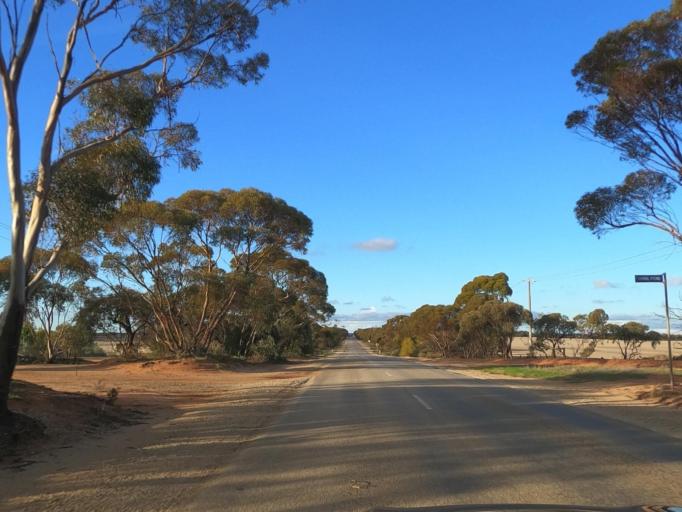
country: AU
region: Victoria
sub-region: Swan Hill
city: Swan Hill
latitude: -35.3489
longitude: 143.5140
